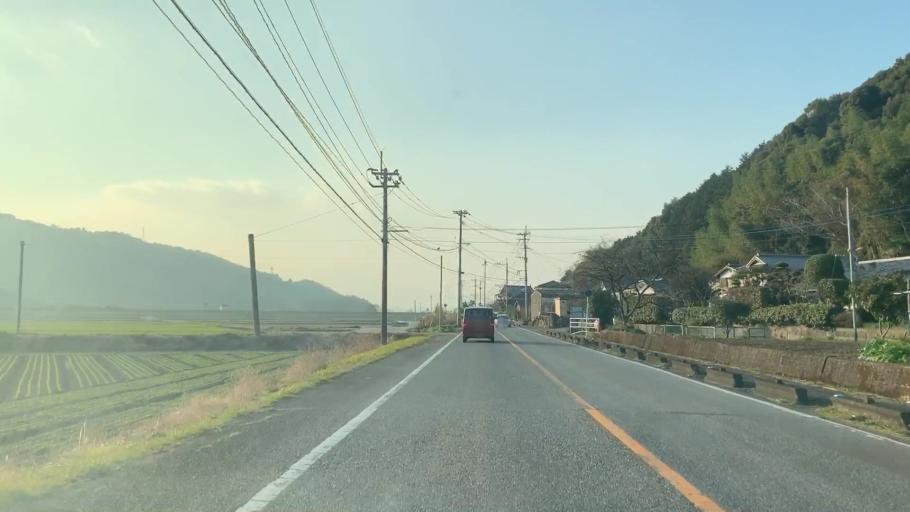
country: JP
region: Saga Prefecture
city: Saga-shi
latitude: 33.2749
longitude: 130.1729
